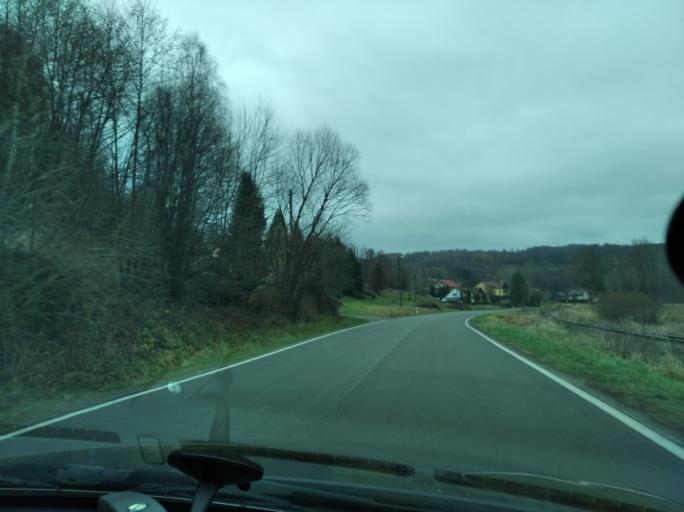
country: PL
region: Subcarpathian Voivodeship
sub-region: Powiat przeworski
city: Jawornik Polski
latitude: 49.9193
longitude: 22.3038
